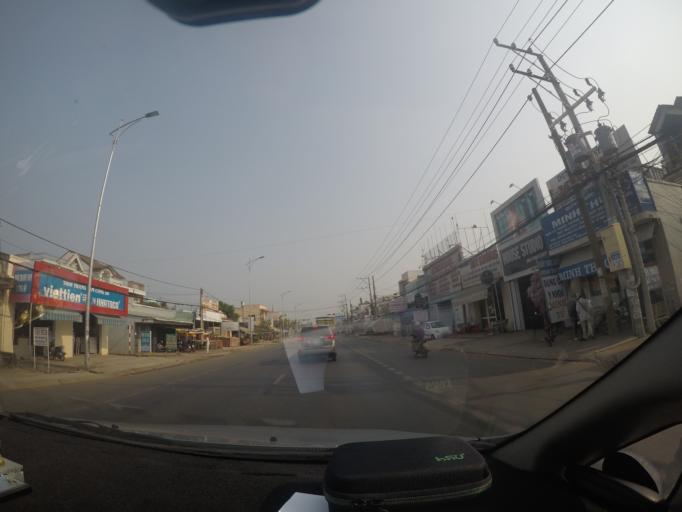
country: VN
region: Dong Nai
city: Thong Nhat
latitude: 11.0243
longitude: 107.1755
